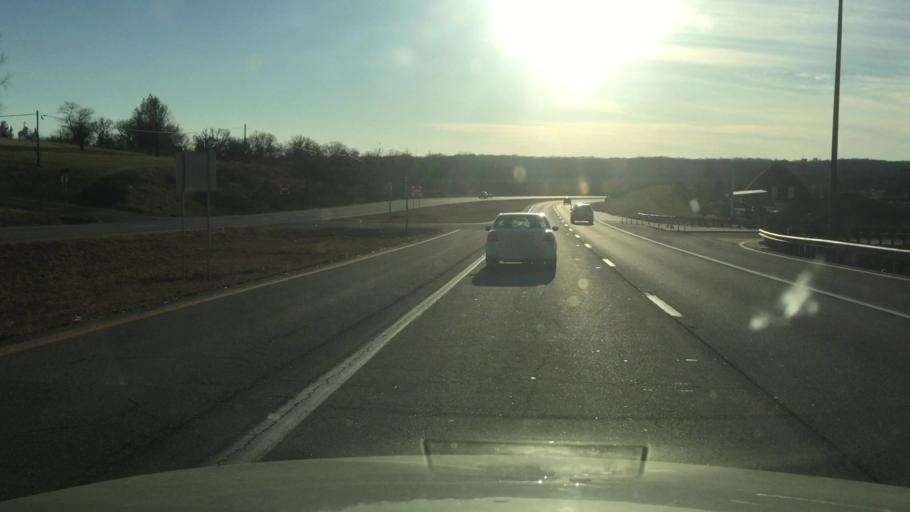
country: US
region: Missouri
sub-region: Cole County
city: Wardsville
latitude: 38.5114
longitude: -92.2438
